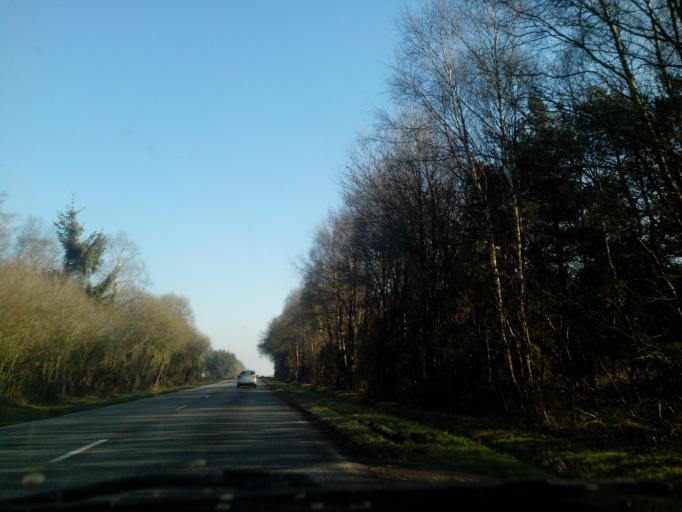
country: FR
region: Brittany
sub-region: Departement des Cotes-d'Armor
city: Merdrignac
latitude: 48.1976
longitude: -2.4721
